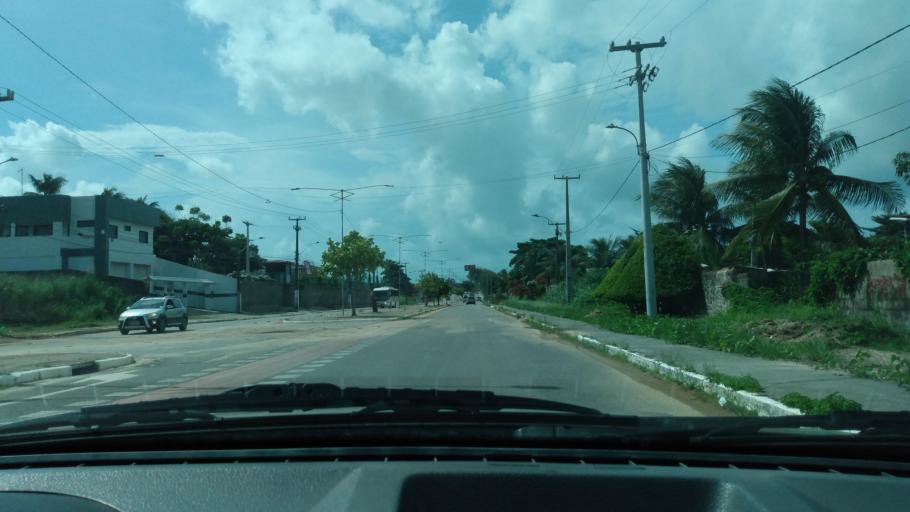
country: BR
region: Pernambuco
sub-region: Cabo De Santo Agostinho
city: Cabo
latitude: -8.3153
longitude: -34.9498
